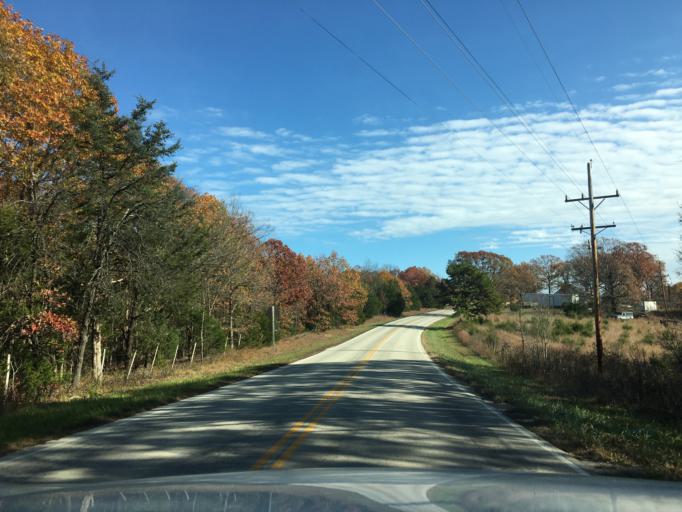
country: US
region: Missouri
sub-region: Maries County
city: Belle
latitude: 38.3118
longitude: -91.7428
